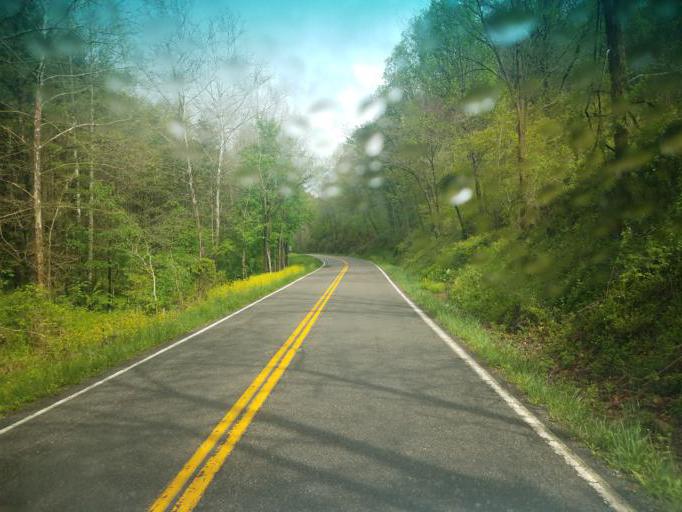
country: US
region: Virginia
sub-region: Smyth County
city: Marion
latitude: 36.9387
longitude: -81.5272
